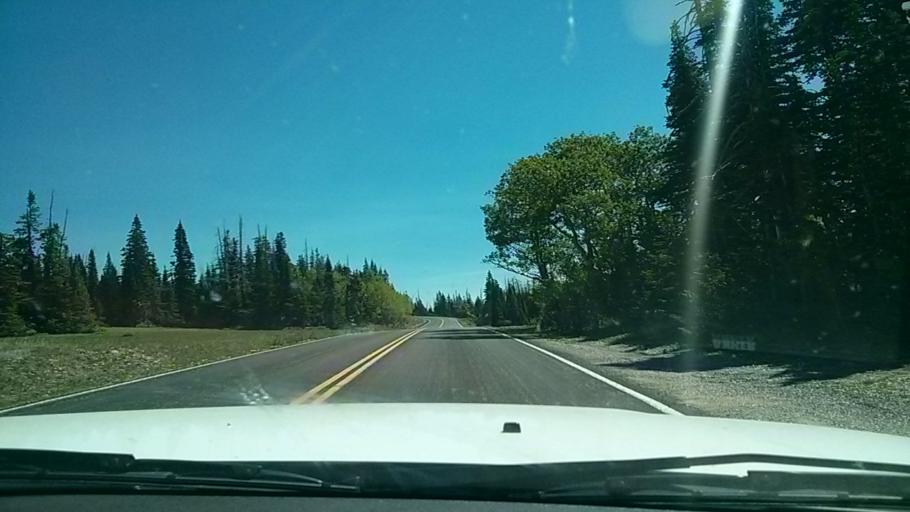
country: US
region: Utah
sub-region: Iron County
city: Parowan
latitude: 37.6334
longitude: -112.8258
